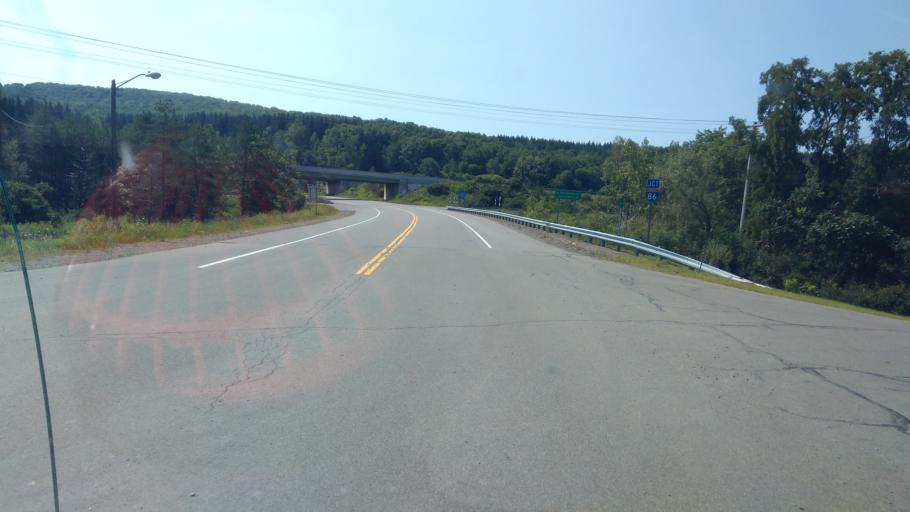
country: US
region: New York
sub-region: Allegany County
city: Belmont
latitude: 42.3023
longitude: -78.0122
